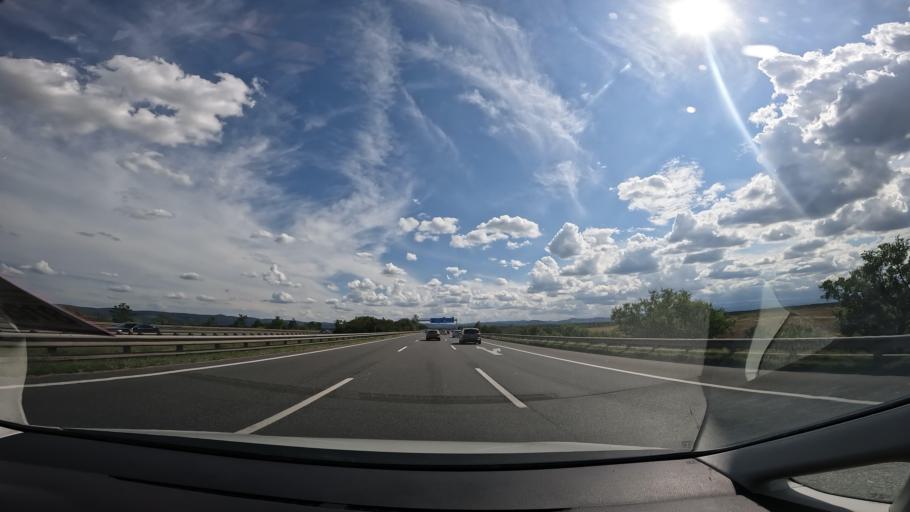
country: AT
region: Lower Austria
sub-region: Wiener Neustadt Stadt
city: Wiener Neustadt
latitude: 47.7926
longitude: 16.2024
